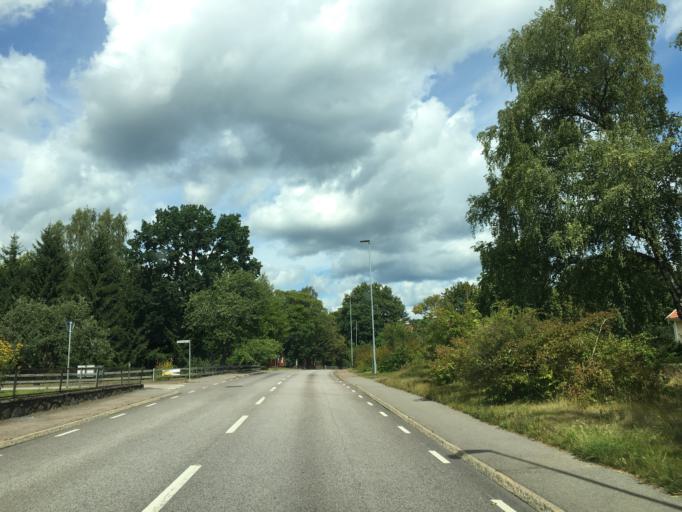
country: SE
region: Kalmar
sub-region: Nybro Kommun
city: Nybro
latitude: 56.9379
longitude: 15.9127
